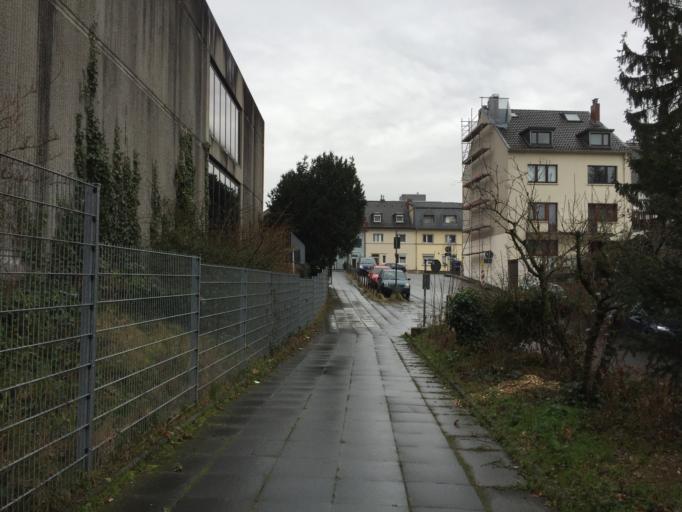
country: DE
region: North Rhine-Westphalia
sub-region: Regierungsbezirk Koln
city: Bonn
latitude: 50.7527
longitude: 7.0963
